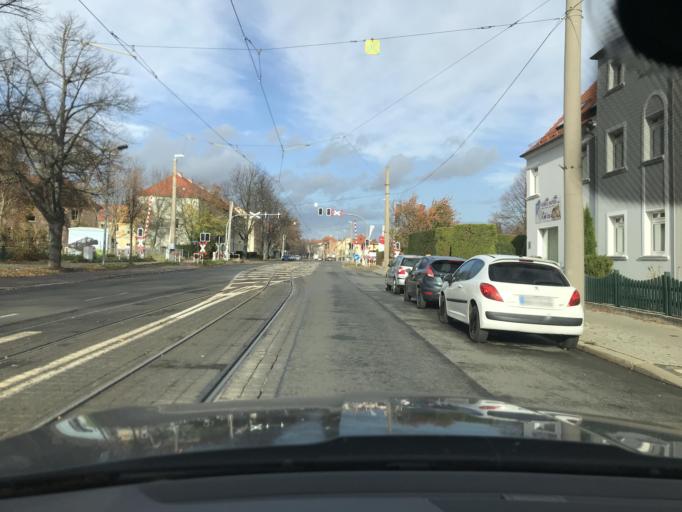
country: DE
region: Saxony-Anhalt
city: Halberstadt
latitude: 51.8831
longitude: 11.0563
